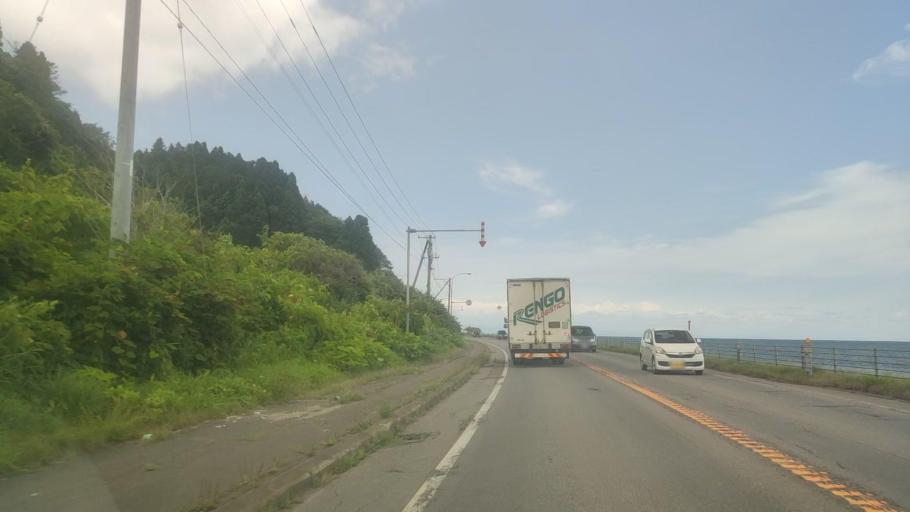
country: JP
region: Hokkaido
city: Nanae
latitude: 42.1459
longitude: 140.4995
